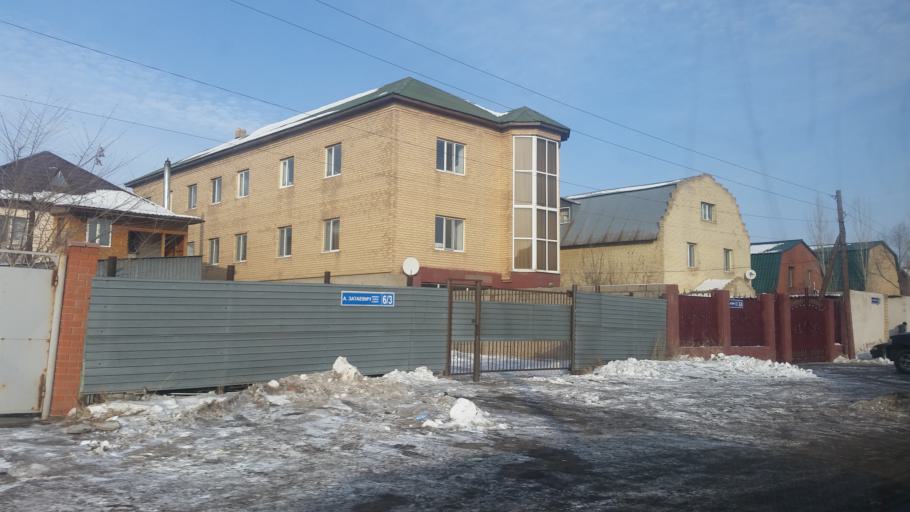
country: KZ
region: Astana Qalasy
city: Astana
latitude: 51.1877
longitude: 71.3991
